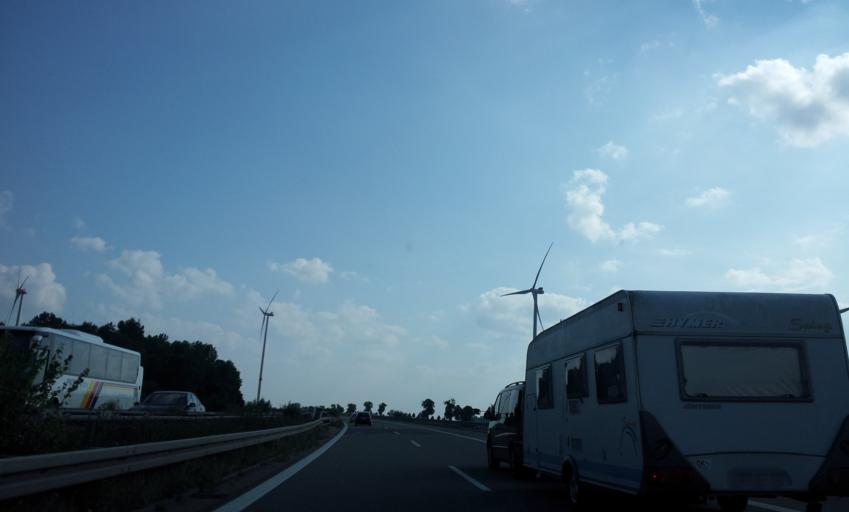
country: DE
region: Mecklenburg-Vorpommern
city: Jarmen
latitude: 53.8982
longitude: 13.3430
